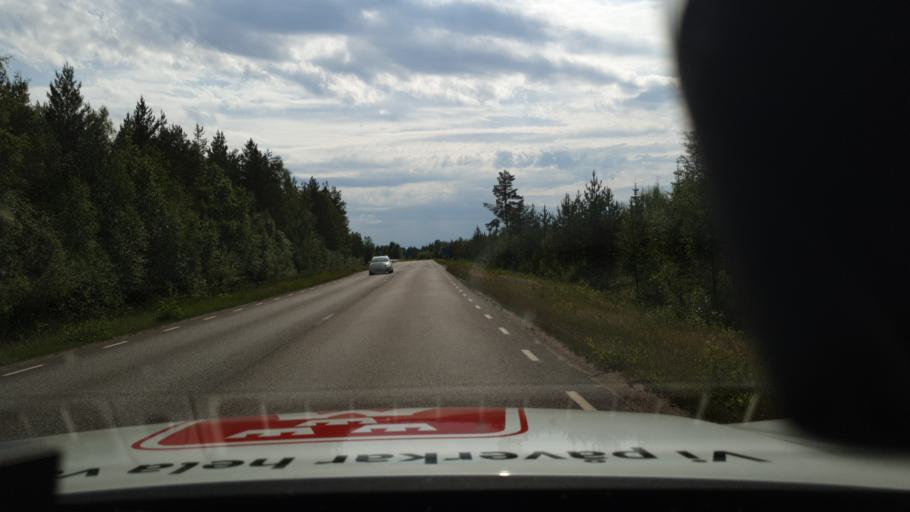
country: SE
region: Norrbotten
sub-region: Lulea Kommun
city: Ranea
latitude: 65.8445
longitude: 22.2651
